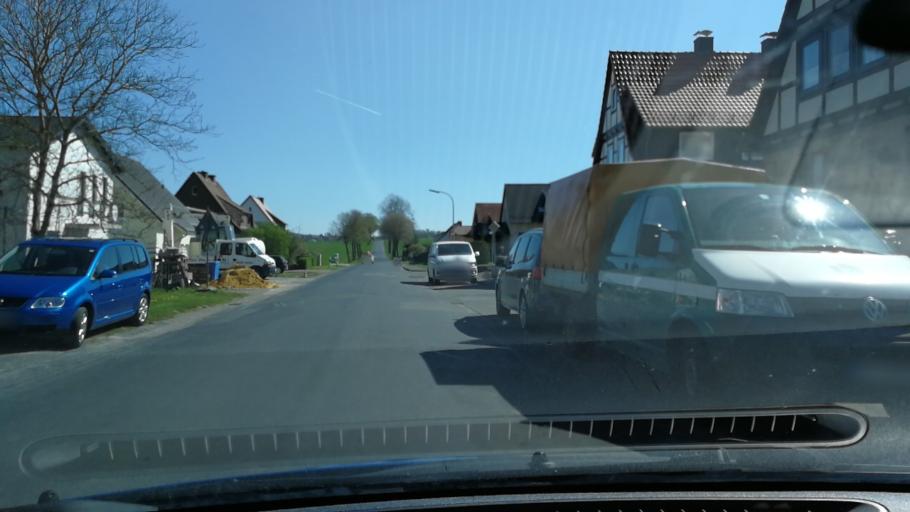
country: DE
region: Lower Saxony
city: Buhren
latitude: 51.5201
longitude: 9.7076
